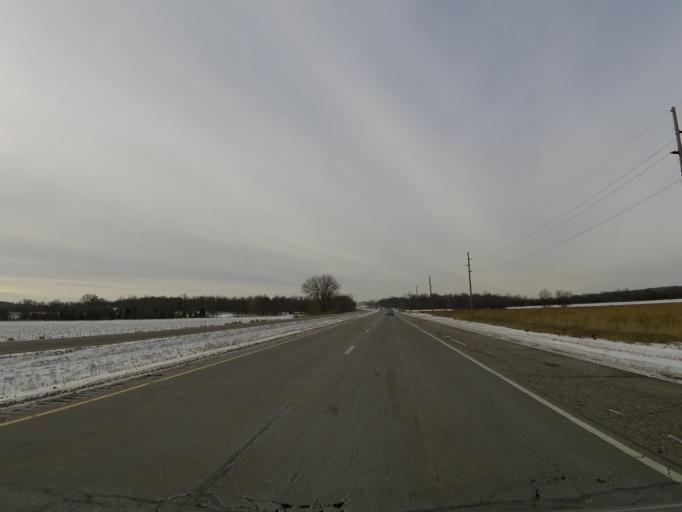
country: US
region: Minnesota
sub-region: Scott County
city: Belle Plaine
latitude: 44.6472
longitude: -93.7020
